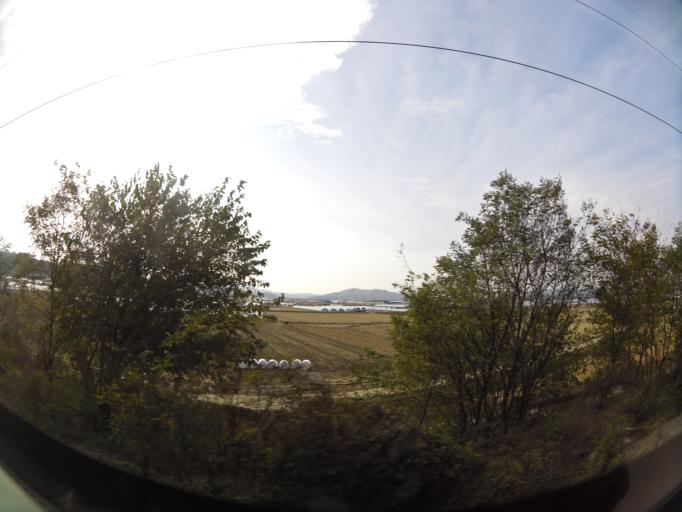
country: KR
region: Daejeon
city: Songgang-dong
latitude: 36.5615
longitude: 127.3217
